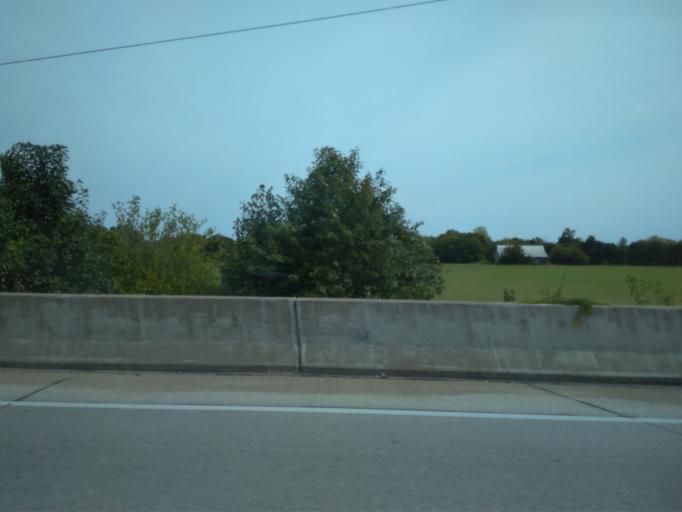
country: US
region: Kentucky
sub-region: Jefferson County
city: Saint Regis Park
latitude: 38.2375
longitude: -85.6195
